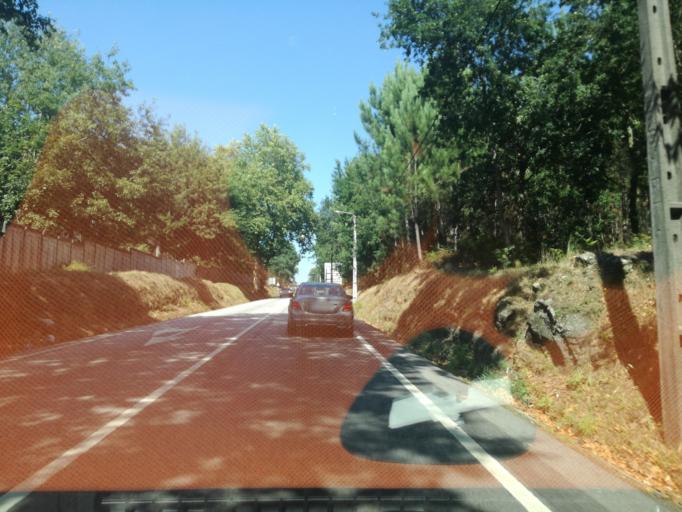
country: PT
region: Viana do Castelo
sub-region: Viana do Castelo
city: Darque
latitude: 41.6678
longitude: -8.7826
